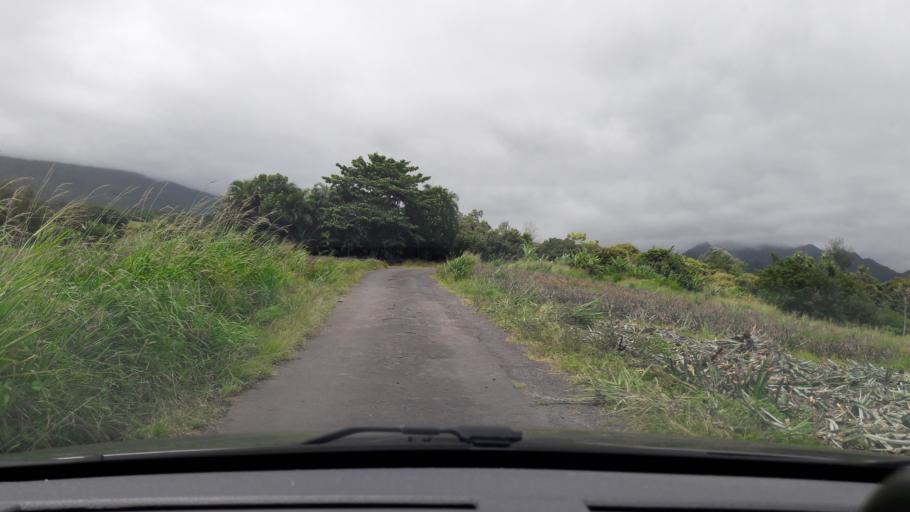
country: RE
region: Reunion
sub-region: Reunion
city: Saint-Benoit
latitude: -21.0964
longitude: 55.6996
